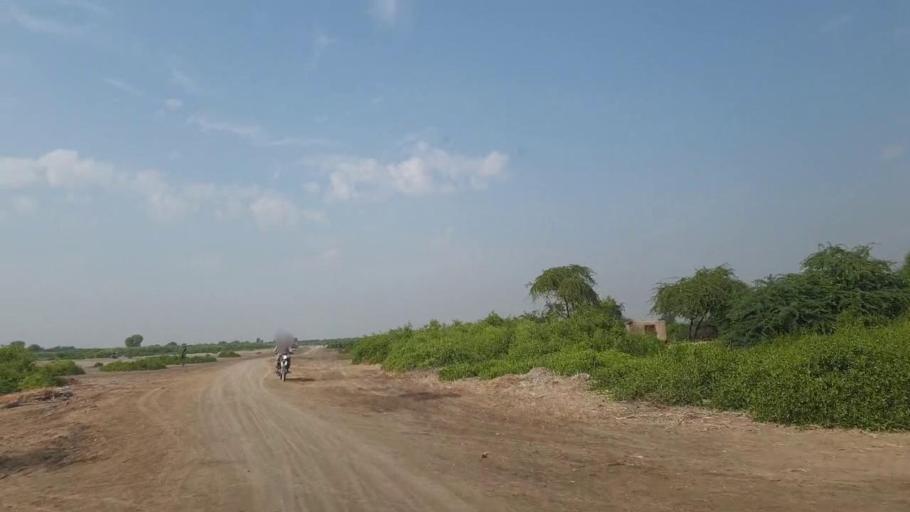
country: PK
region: Sindh
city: Digri
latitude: 25.0306
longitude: 69.0710
